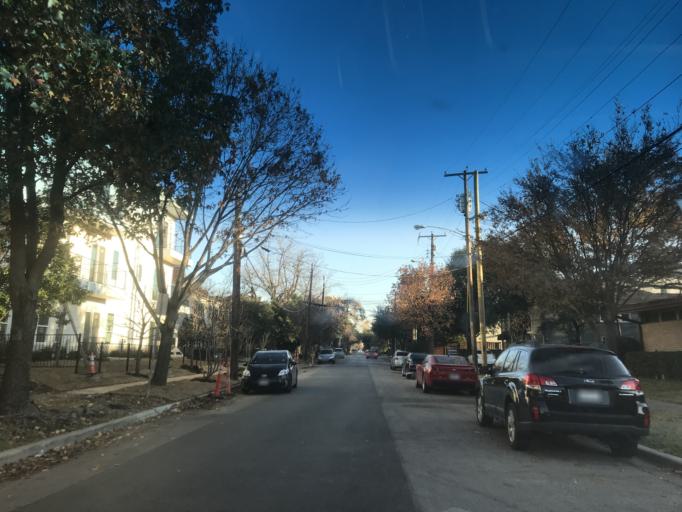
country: US
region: Texas
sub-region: Dallas County
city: Highland Park
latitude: 32.8148
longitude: -96.8111
